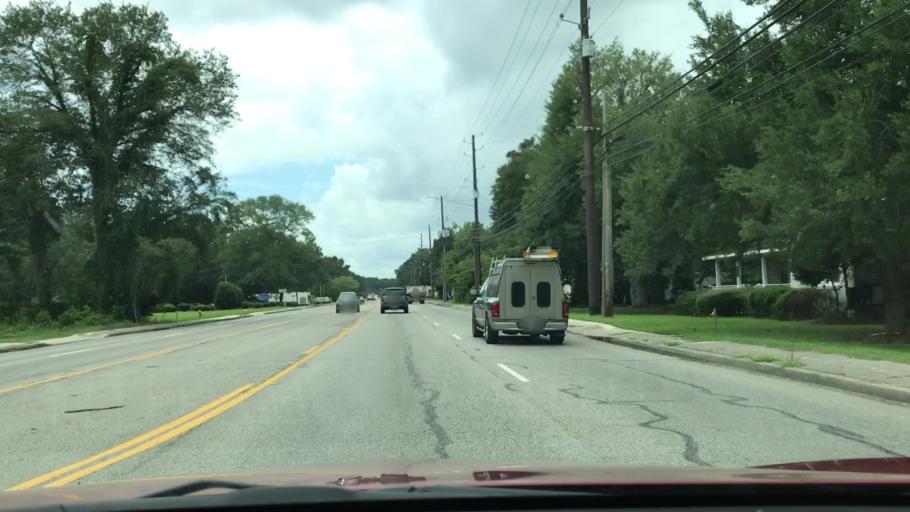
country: US
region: South Carolina
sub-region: Georgetown County
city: Georgetown
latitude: 33.4066
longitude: -79.2874
